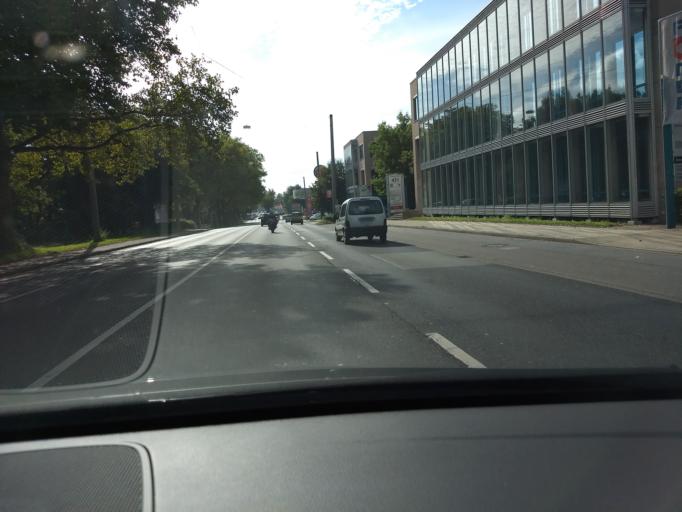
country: DE
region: North Rhine-Westphalia
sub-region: Regierungsbezirk Dusseldorf
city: Essen
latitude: 51.4908
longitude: 6.9979
